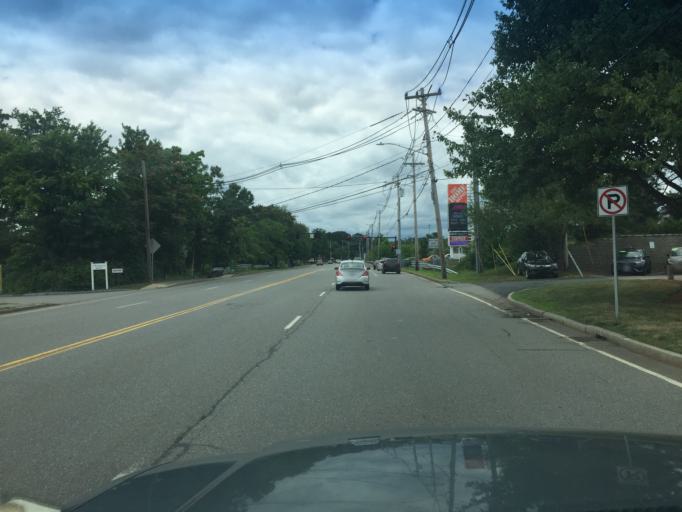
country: US
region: Massachusetts
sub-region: Middlesex County
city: Reading
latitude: 42.5180
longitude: -71.0916
